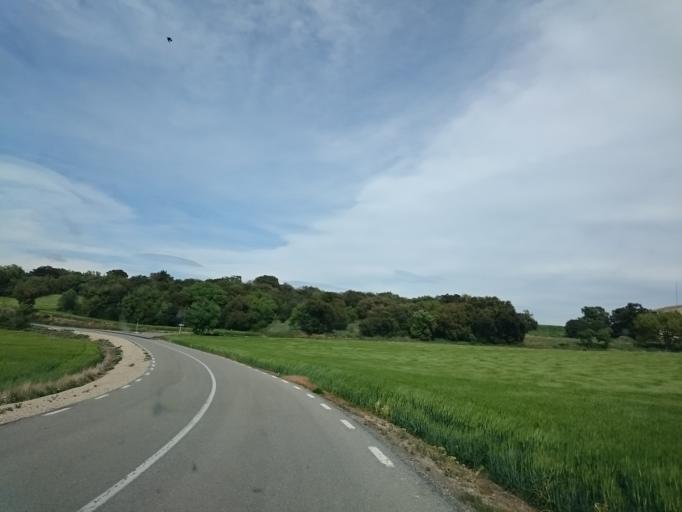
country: ES
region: Catalonia
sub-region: Provincia de Barcelona
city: Calaf
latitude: 41.7230
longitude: 1.4695
